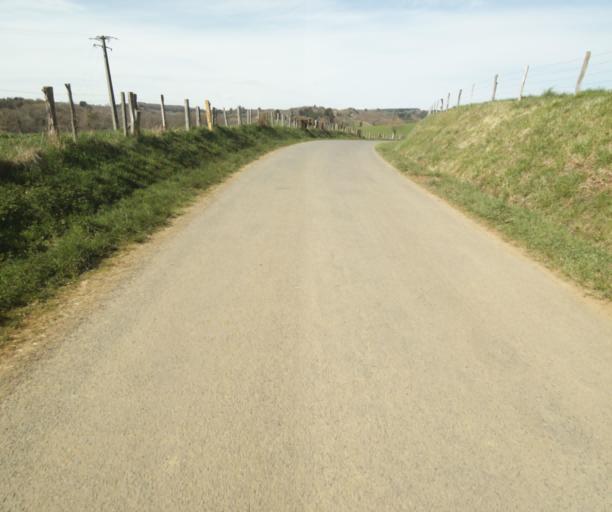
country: FR
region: Limousin
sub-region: Departement de la Correze
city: Seilhac
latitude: 45.3783
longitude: 1.7769
